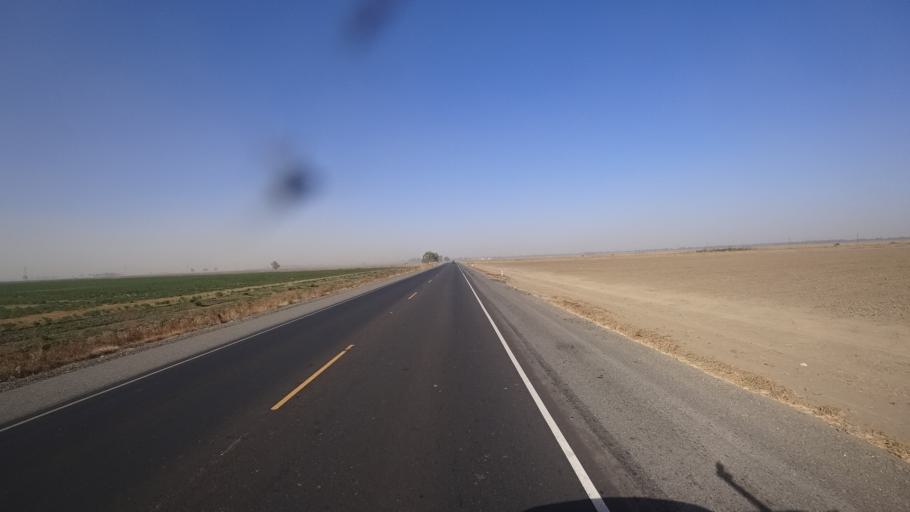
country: US
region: California
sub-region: Yolo County
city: Woodland
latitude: 38.7613
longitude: -121.7290
